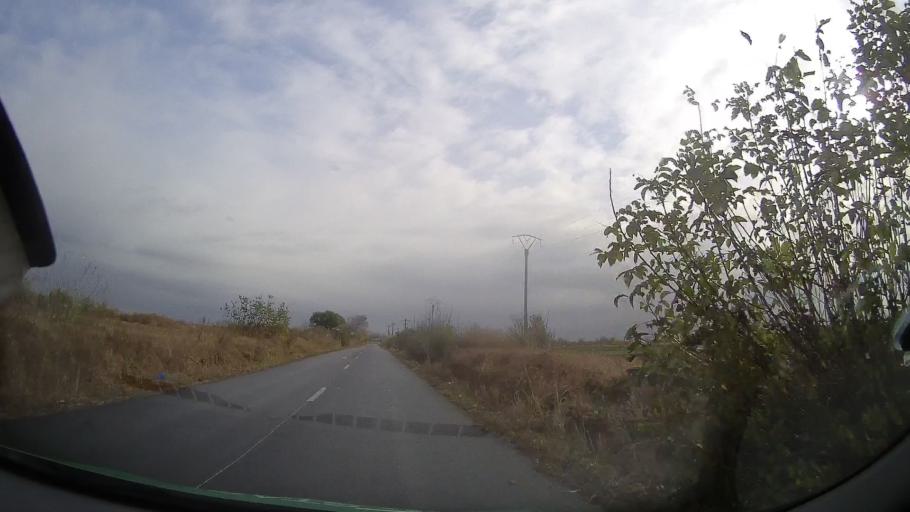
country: RO
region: Ialomita
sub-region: Comuna Maia
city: Maia
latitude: 44.7464
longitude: 26.3973
